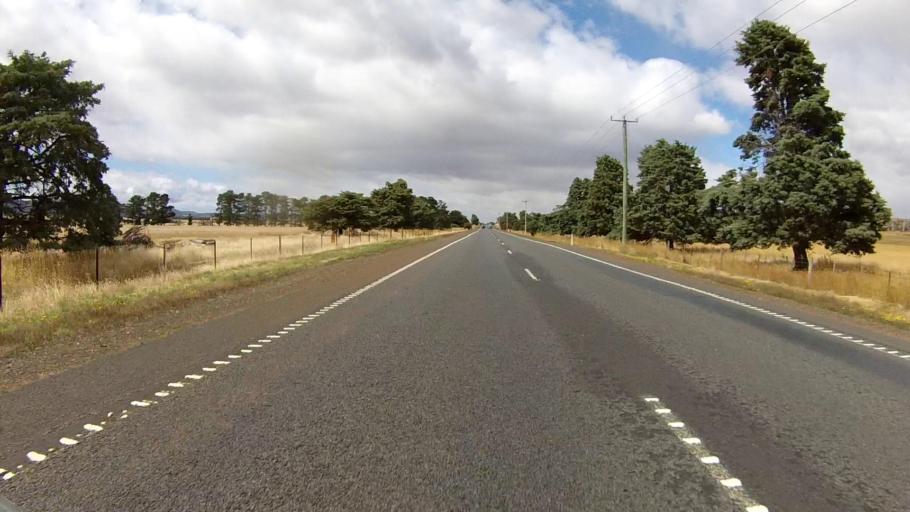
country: AU
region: Tasmania
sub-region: Northern Midlands
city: Evandale
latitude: -41.9490
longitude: 147.4942
